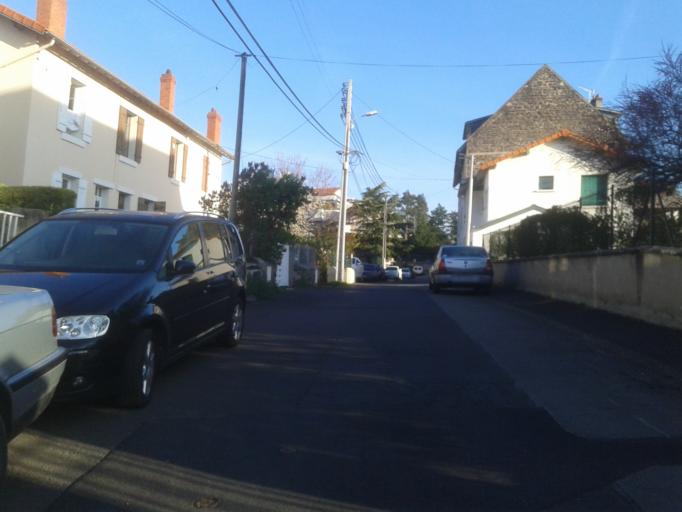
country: FR
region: Auvergne
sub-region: Departement du Puy-de-Dome
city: Chamalieres
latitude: 45.7683
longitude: 3.0640
